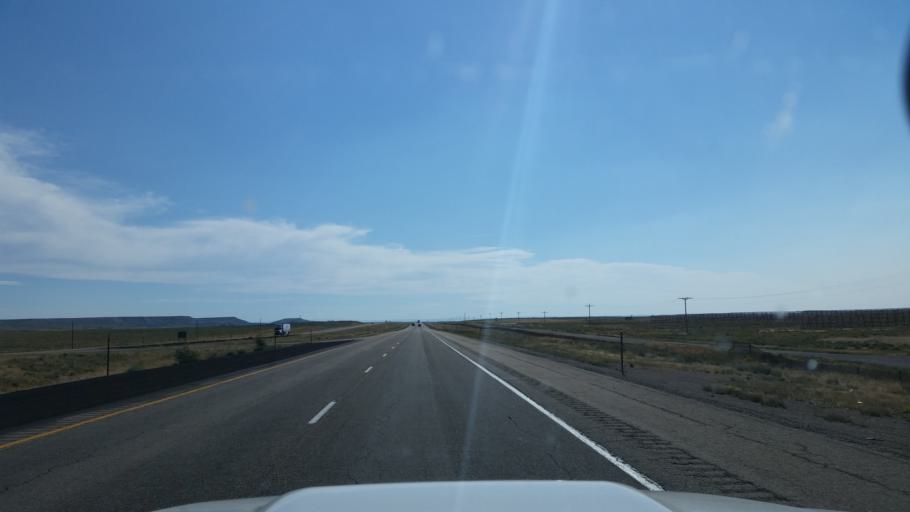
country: US
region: Wyoming
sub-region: Uinta County
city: Lyman
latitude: 41.4606
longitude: -110.0566
